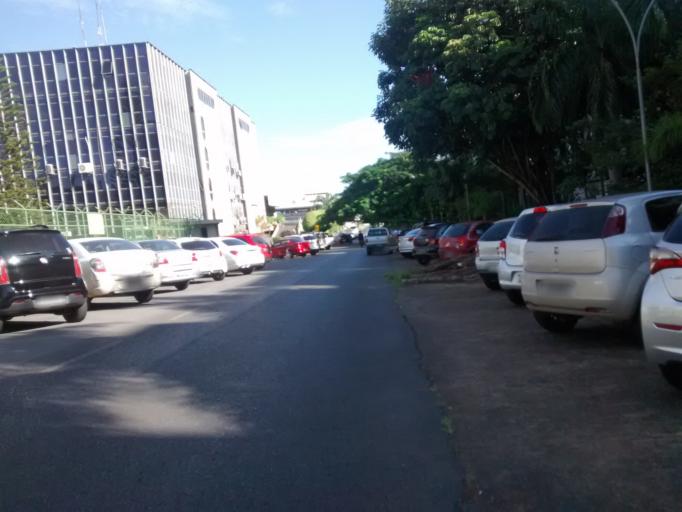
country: BR
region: Federal District
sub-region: Brasilia
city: Brasilia
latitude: -15.7593
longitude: -47.8918
